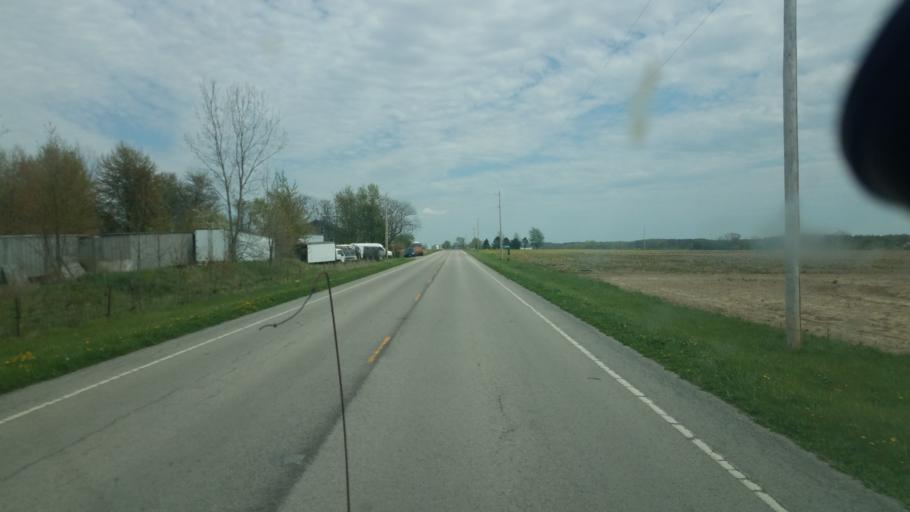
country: US
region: Ohio
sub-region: Hancock County
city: Arlington
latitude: 40.8339
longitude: -83.7317
